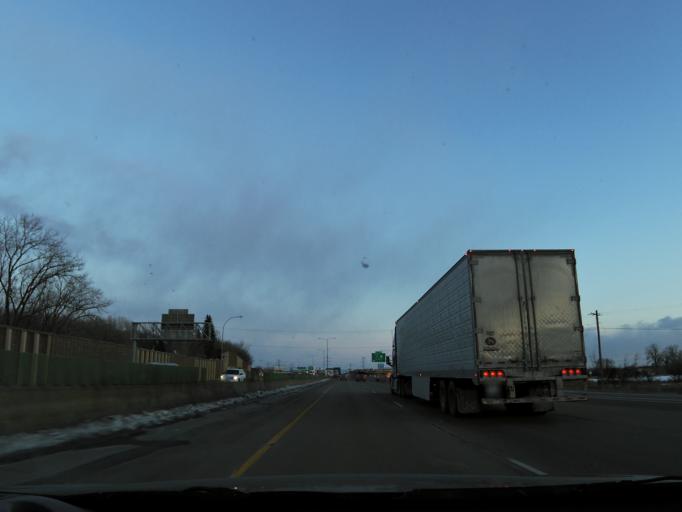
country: US
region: Minnesota
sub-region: Ramsey County
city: Little Canada
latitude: 45.0431
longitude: -93.1033
